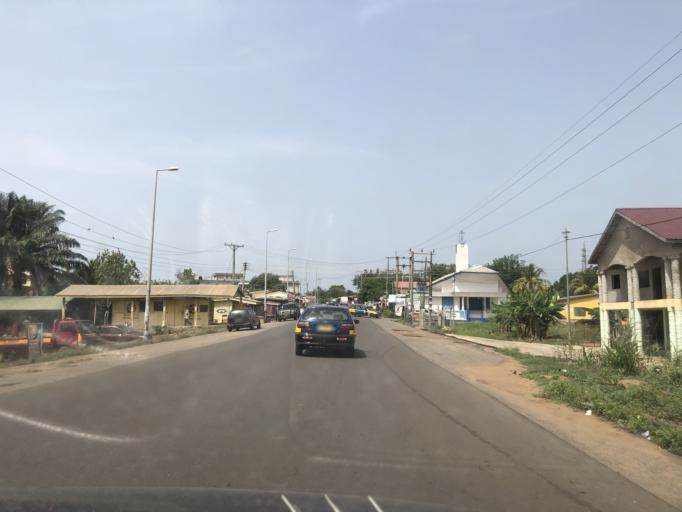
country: GH
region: Eastern
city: Koforidua
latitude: 6.0962
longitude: -0.2671
